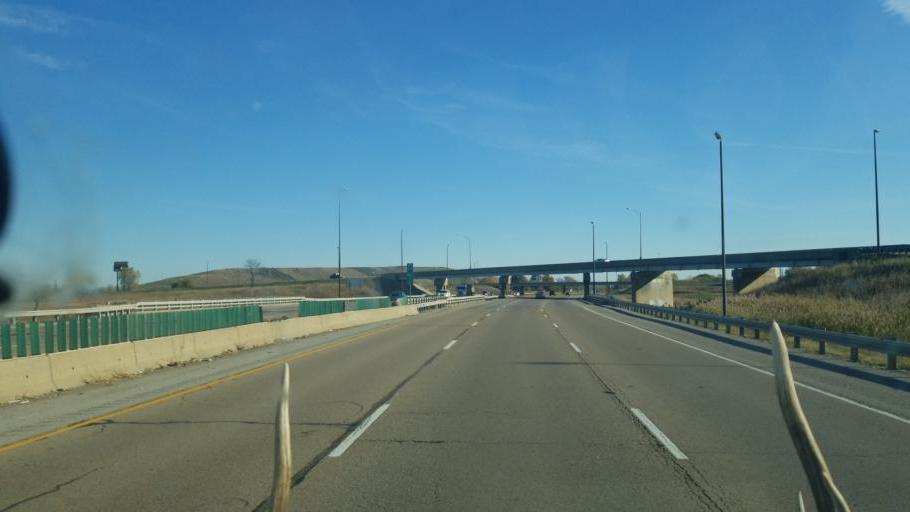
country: US
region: Illinois
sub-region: Saint Clair County
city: East Saint Louis
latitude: 38.6425
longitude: -90.1320
